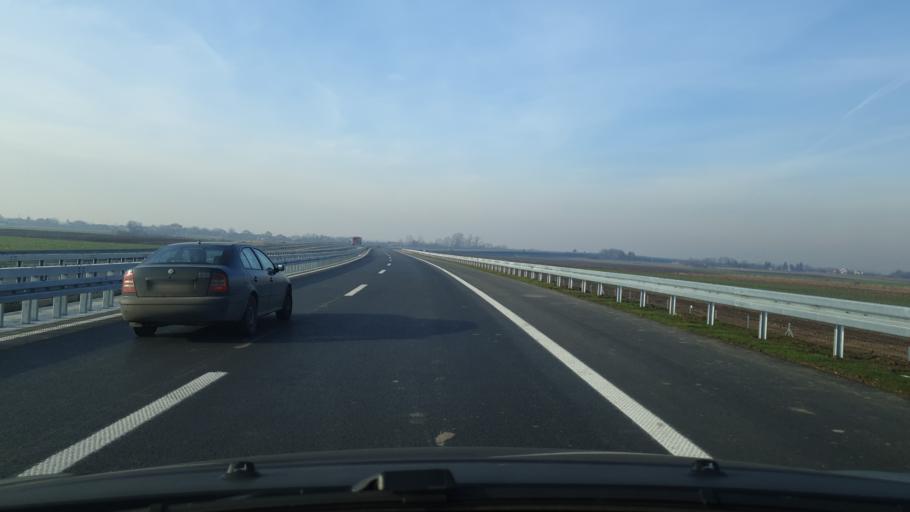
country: RS
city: Boljevci
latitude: 44.7253
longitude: 20.2542
